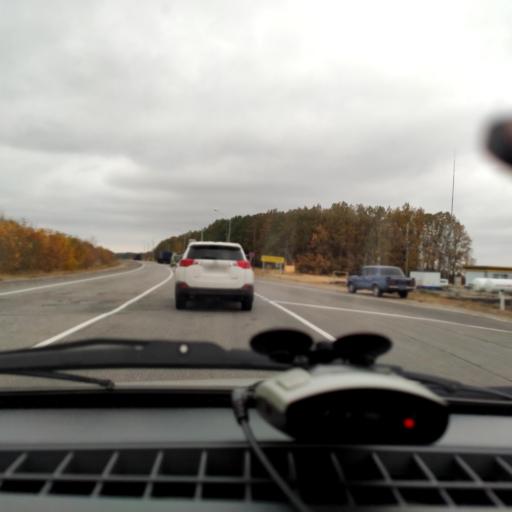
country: RU
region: Voronezj
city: Shilovo
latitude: 51.4273
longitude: 39.0093
